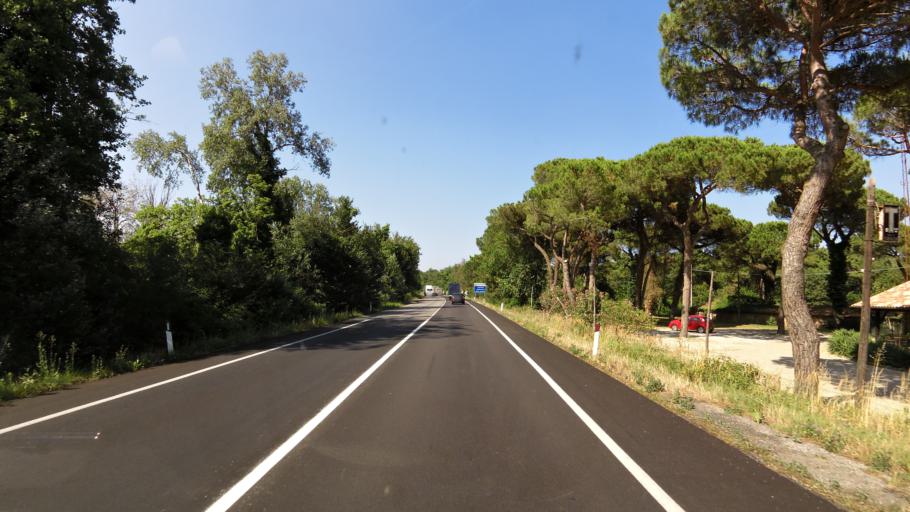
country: IT
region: Emilia-Romagna
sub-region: Provincia di Ravenna
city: Marina Romea
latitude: 44.5134
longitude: 12.2258
